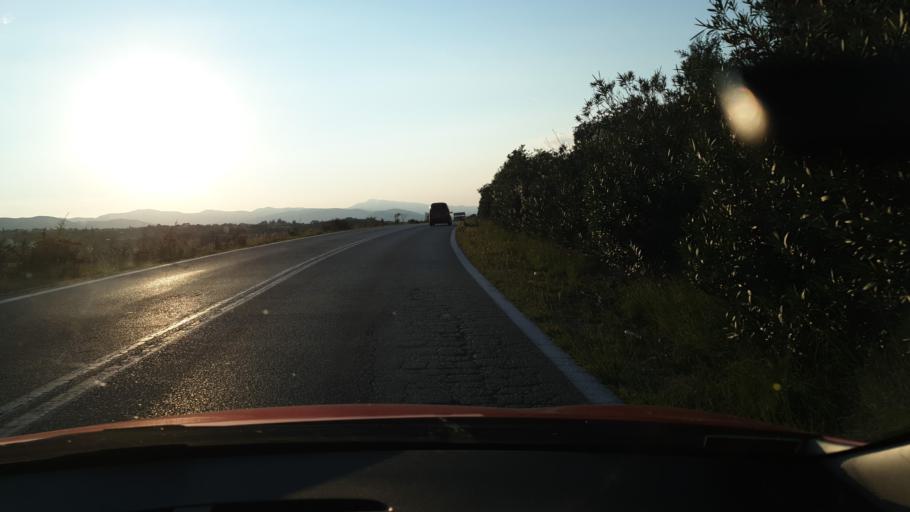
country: GR
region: Central Macedonia
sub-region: Nomos Thessalonikis
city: Nea Apollonia
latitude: 40.5050
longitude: 23.4704
